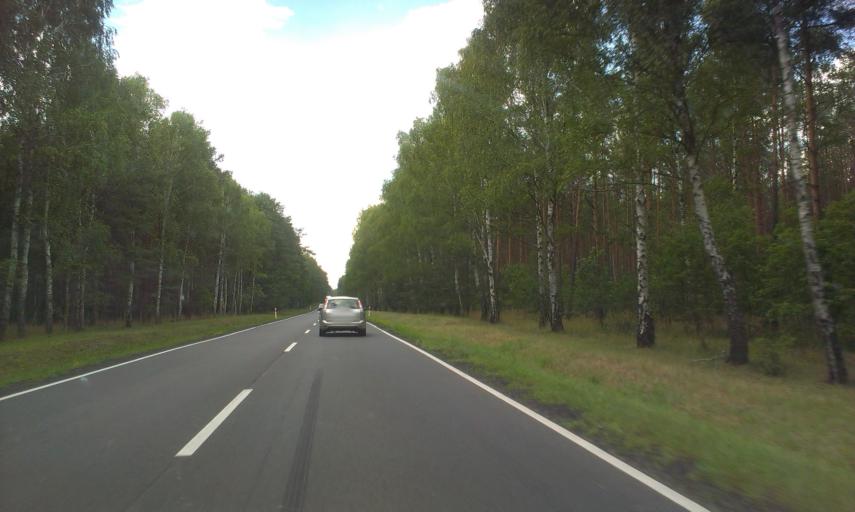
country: PL
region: Greater Poland Voivodeship
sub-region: Powiat zlotowski
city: Tarnowka
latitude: 53.3306
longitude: 16.7940
